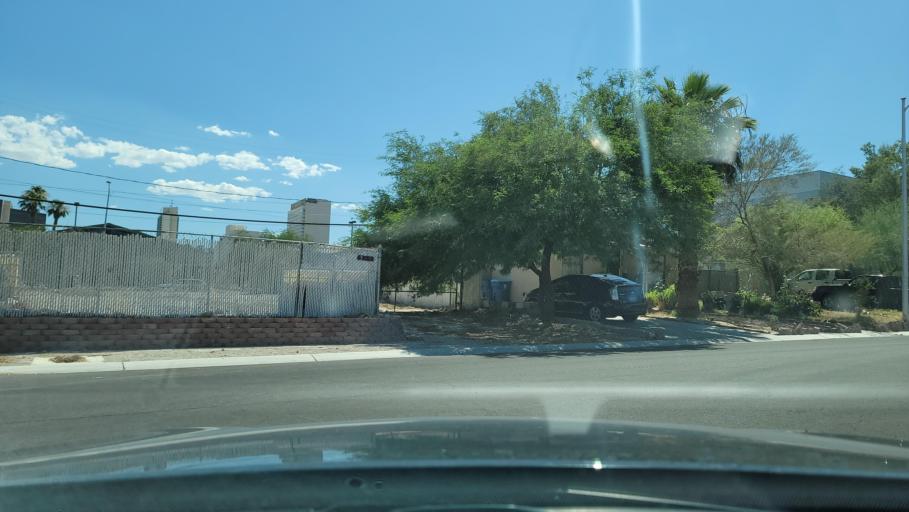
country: US
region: Nevada
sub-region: Clark County
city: Las Vegas
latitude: 36.1758
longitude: -115.1378
